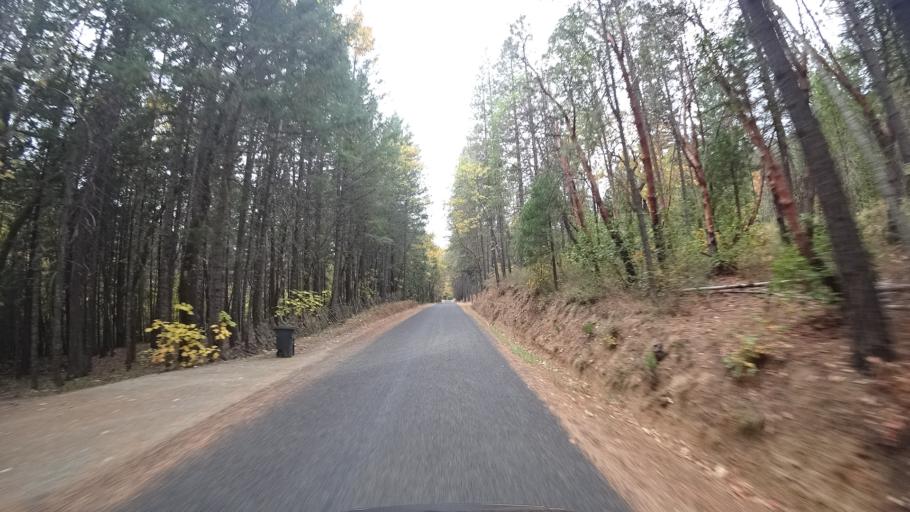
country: US
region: California
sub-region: Siskiyou County
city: Happy Camp
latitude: 41.8603
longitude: -123.1555
